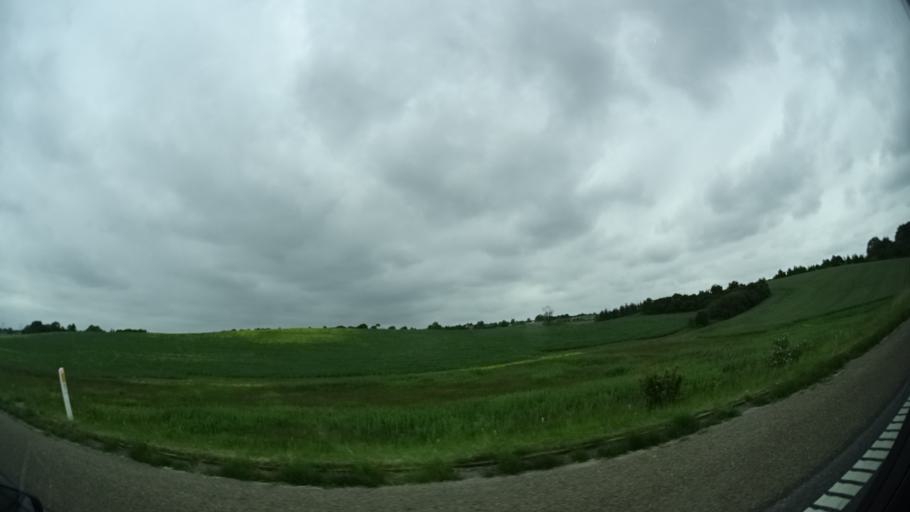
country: DK
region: Central Jutland
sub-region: Arhus Kommune
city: Logten
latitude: 56.2589
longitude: 10.3208
